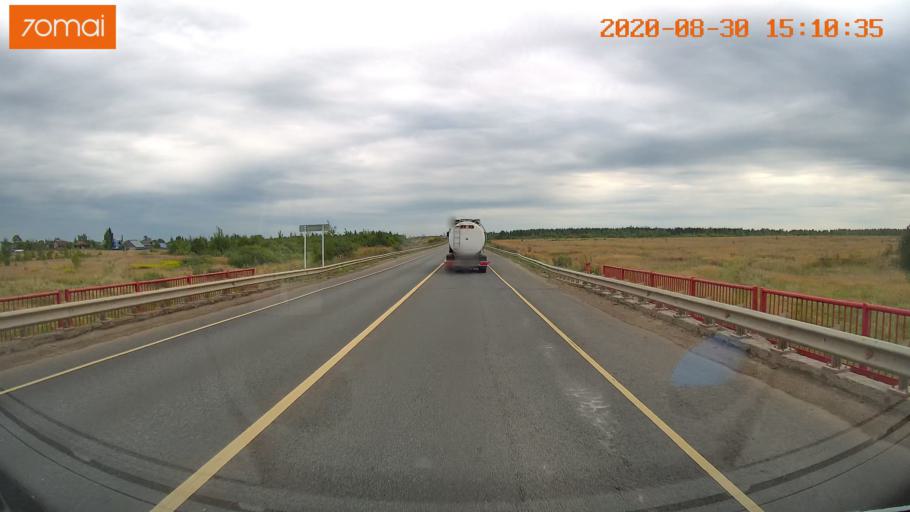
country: RU
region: Ivanovo
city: Staraya Vichuga
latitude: 57.2161
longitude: 41.8640
